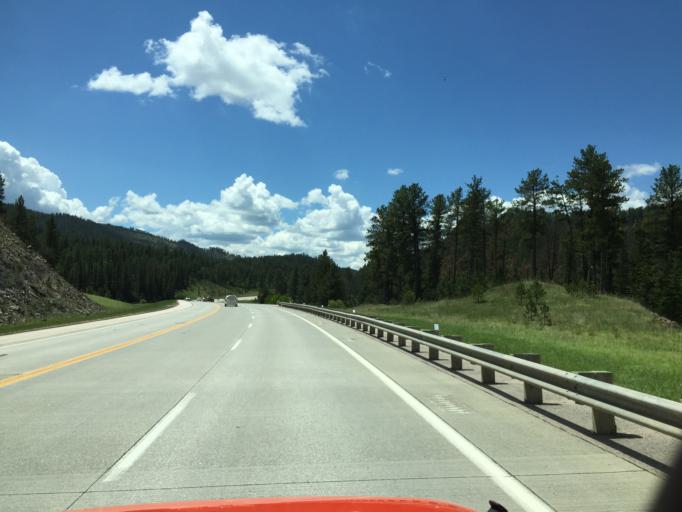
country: US
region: South Dakota
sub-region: Custer County
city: Custer
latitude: 43.8779
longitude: -103.6133
